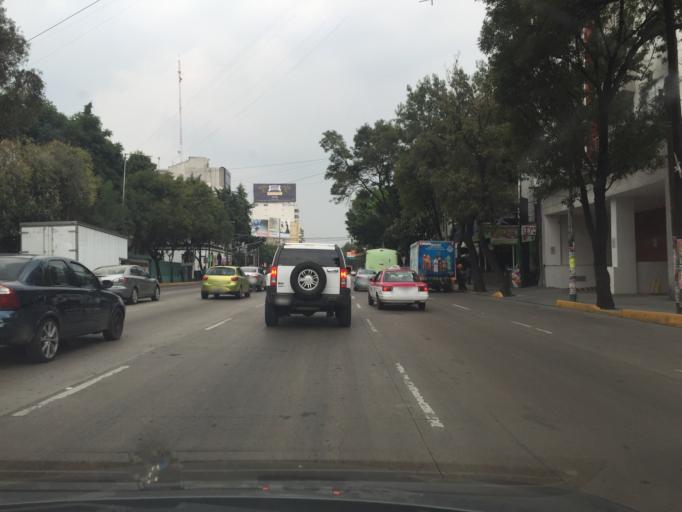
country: MX
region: Mexico City
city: Colonia del Valle
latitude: 19.3933
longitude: -99.1857
